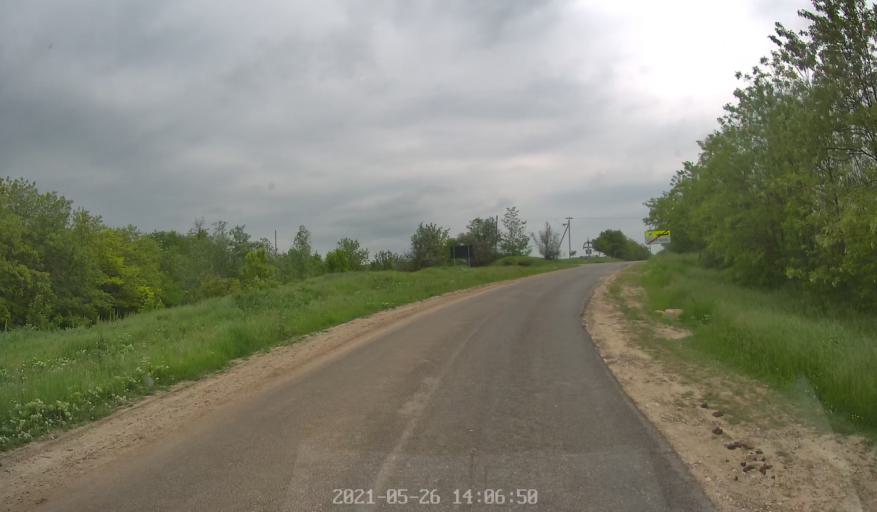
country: MD
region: Hincesti
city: Dancu
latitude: 46.7514
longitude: 28.3570
